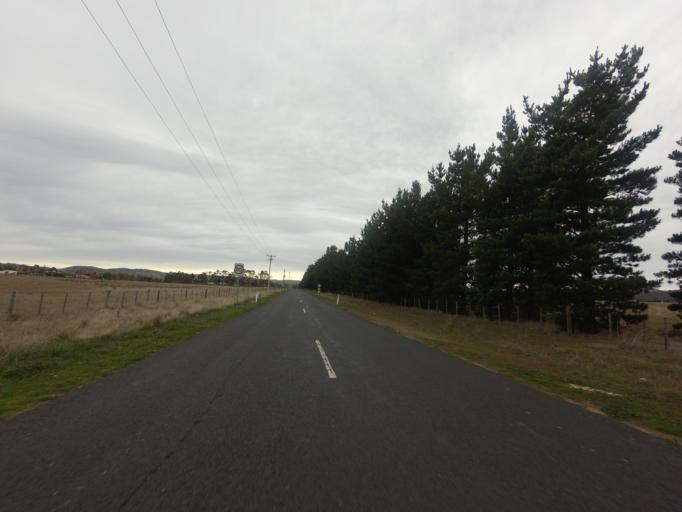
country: AU
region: Tasmania
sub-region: Derwent Valley
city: New Norfolk
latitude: -42.3913
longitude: 147.0056
